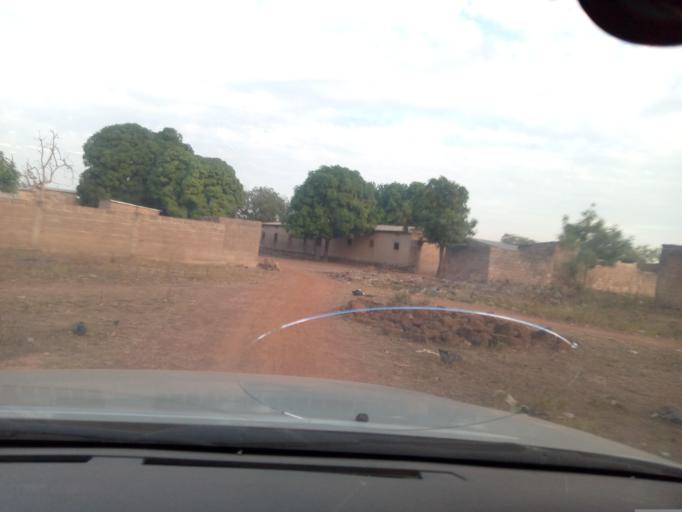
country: ML
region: Sikasso
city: Kadiolo
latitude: 10.5530
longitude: -5.7769
